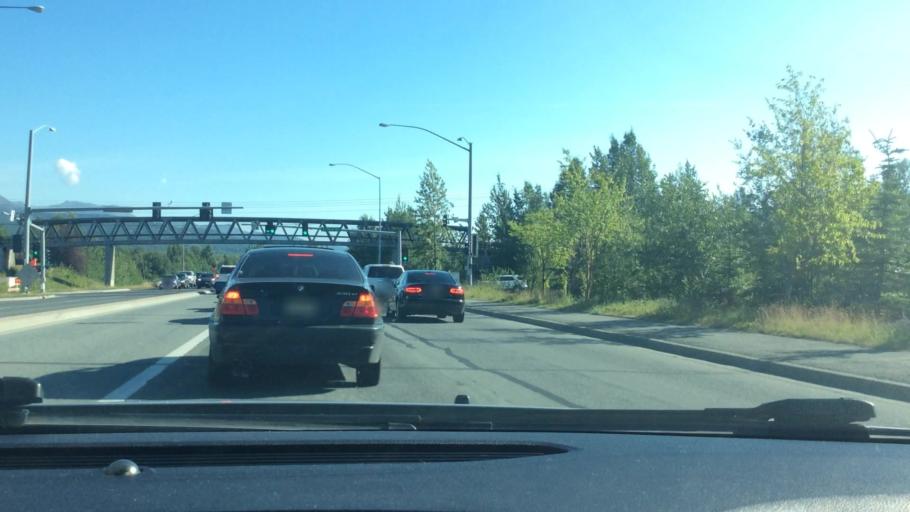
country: US
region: Alaska
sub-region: Anchorage Municipality
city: Elmendorf Air Force Base
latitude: 61.1889
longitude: -149.7334
